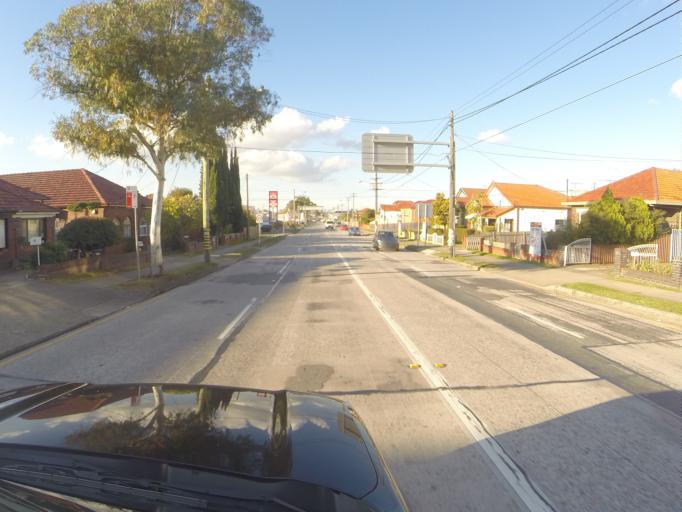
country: AU
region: New South Wales
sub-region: Canterbury
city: Canterbury
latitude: -33.9180
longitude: 151.1049
